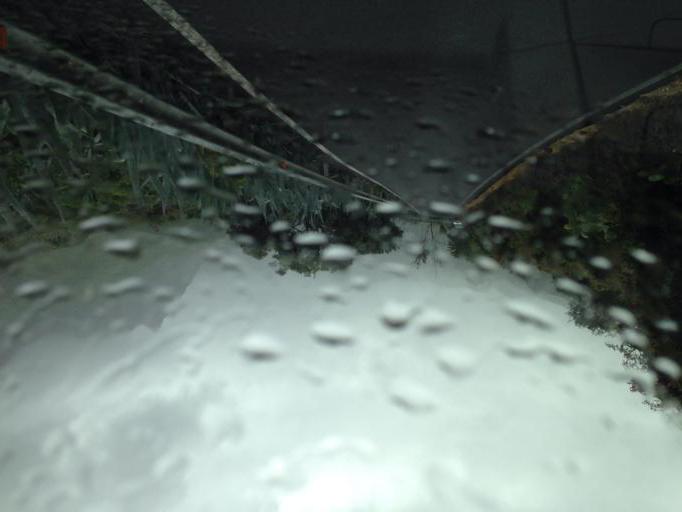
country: ES
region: Canary Islands
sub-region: Provincia de Las Palmas
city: Agaete
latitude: 28.0967
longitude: -15.6889
